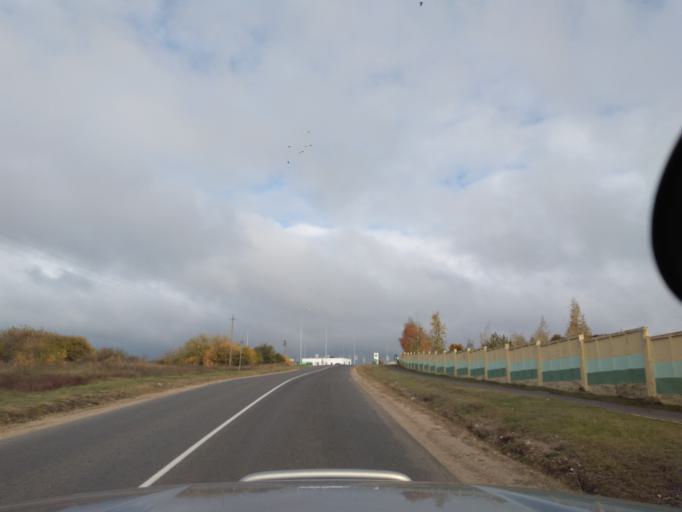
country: BY
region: Minsk
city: Kapyl'
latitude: 53.1468
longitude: 27.0755
